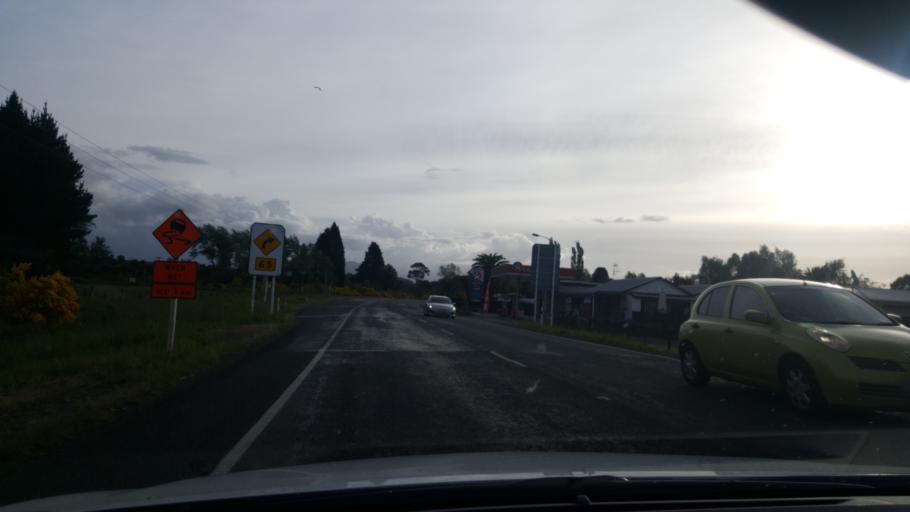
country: NZ
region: Waikato
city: Turangi
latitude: -38.9106
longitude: 175.9040
